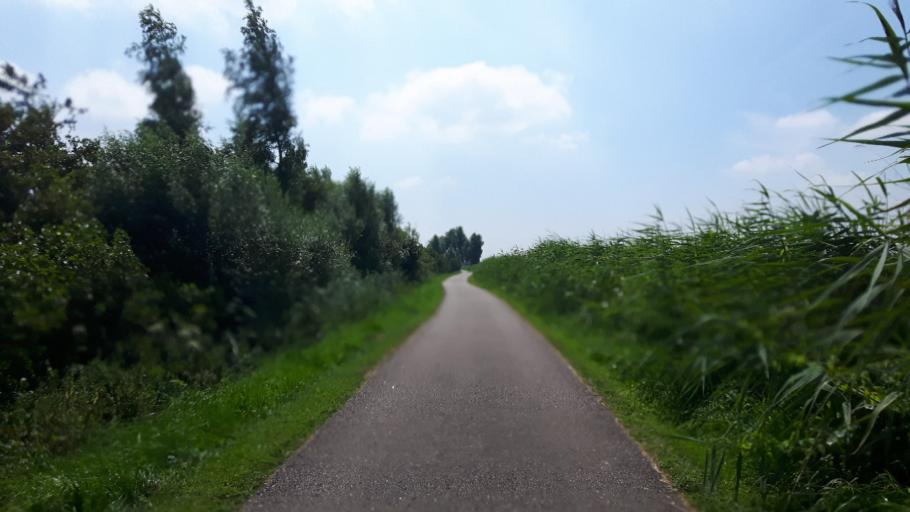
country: NL
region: Utrecht
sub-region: Gemeente Lopik
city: Lopik
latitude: 51.9423
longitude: 4.9998
